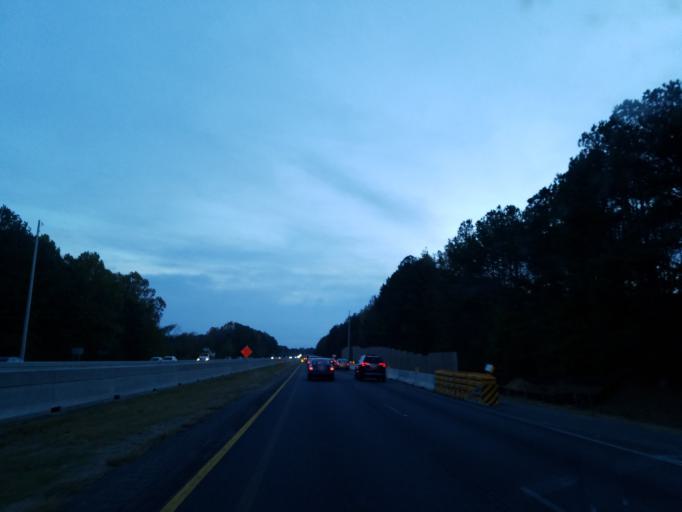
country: US
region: Georgia
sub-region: Cherokee County
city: Woodstock
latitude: 34.0767
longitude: -84.5387
